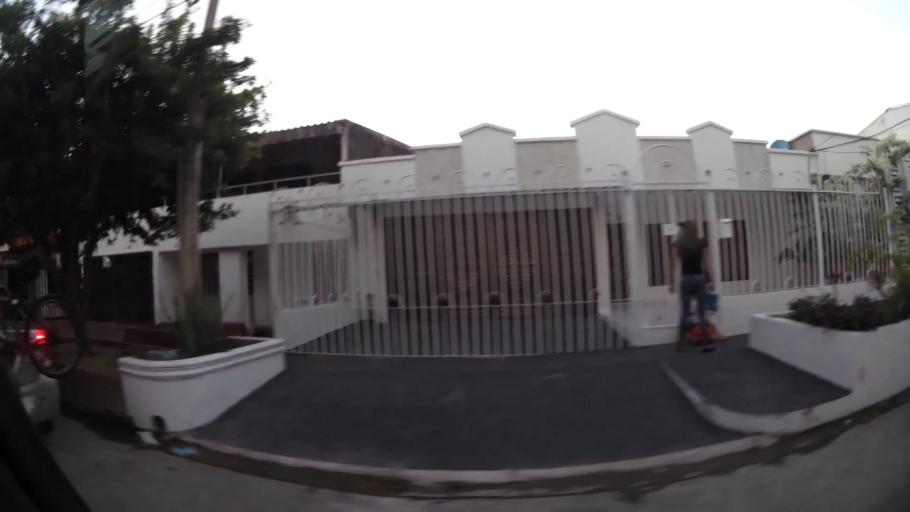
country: CO
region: Atlantico
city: Barranquilla
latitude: 10.9824
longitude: -74.8086
